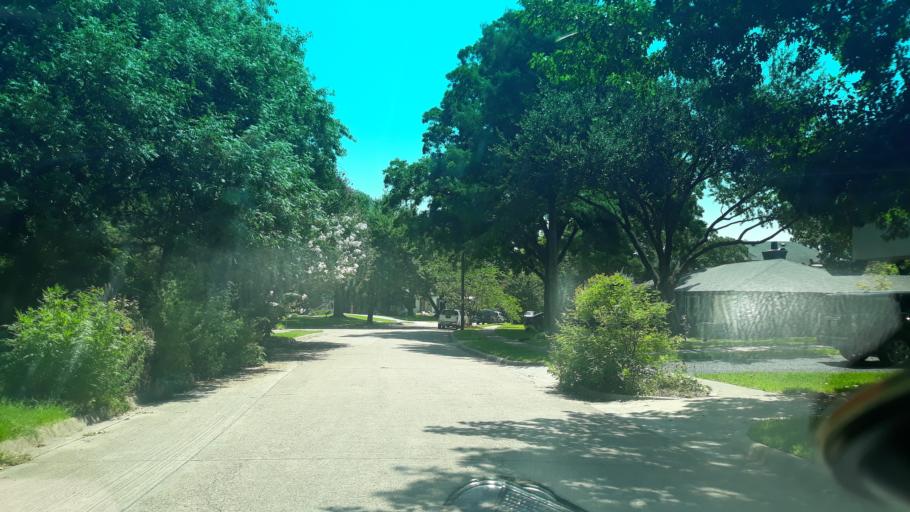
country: US
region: Texas
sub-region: Dallas County
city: Highland Park
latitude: 32.8173
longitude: -96.7340
